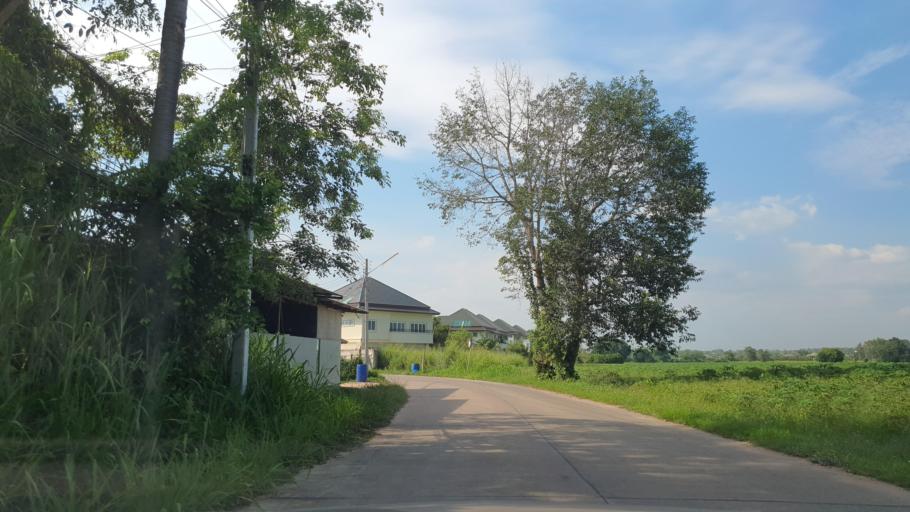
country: TH
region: Chon Buri
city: Sattahip
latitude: 12.7995
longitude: 100.9351
